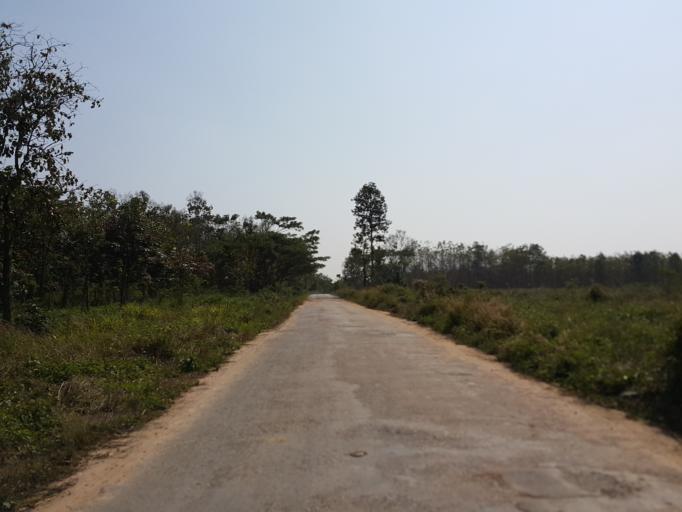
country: TH
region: Lampang
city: Wang Nuea
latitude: 19.0146
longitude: 99.6231
